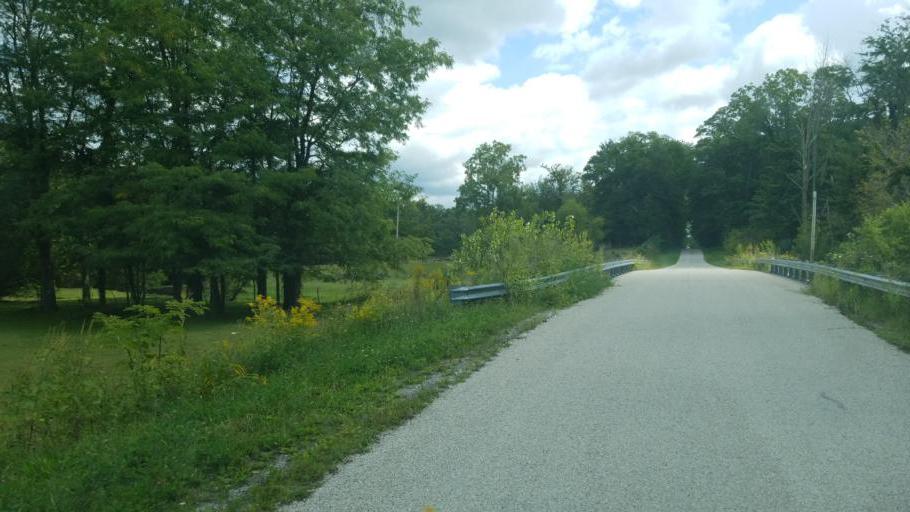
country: US
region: Ohio
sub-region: Huron County
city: Willard
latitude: 41.1164
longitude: -82.8272
